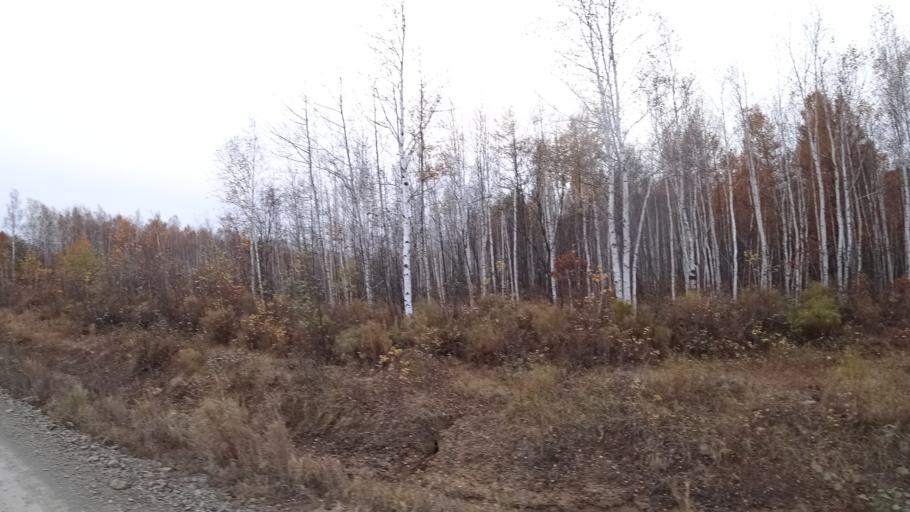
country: RU
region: Khabarovsk Krai
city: Amursk
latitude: 49.9818
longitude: 136.3148
